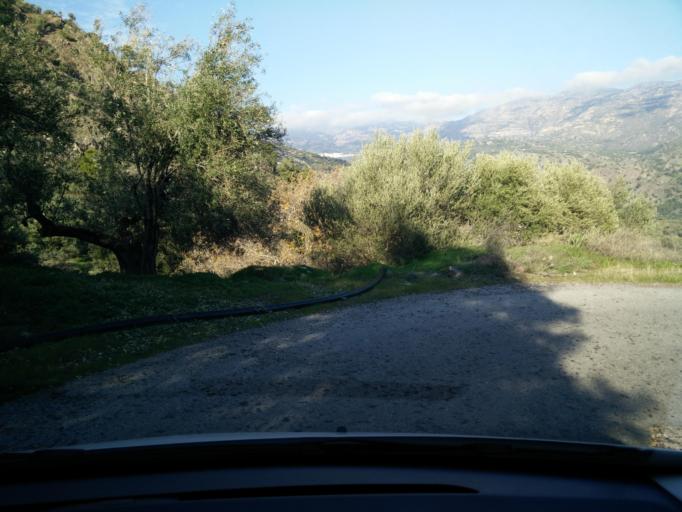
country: GR
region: Crete
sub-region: Nomos Lasithiou
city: Gra Liyia
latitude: 35.0328
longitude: 25.5699
